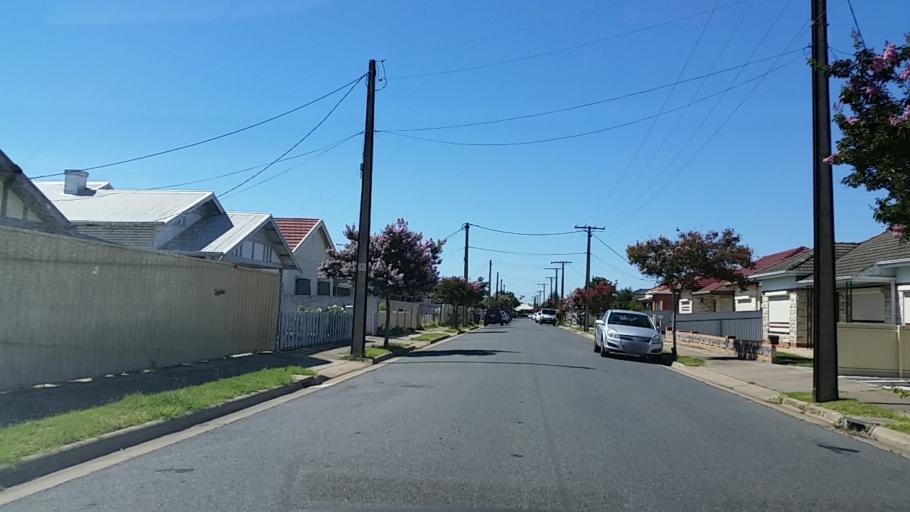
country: AU
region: South Australia
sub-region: Charles Sturt
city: Albert Park
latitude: -34.8717
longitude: 138.5158
